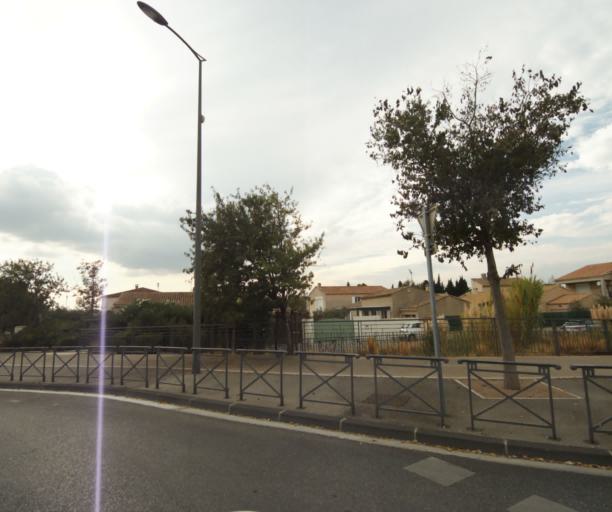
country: FR
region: Provence-Alpes-Cote d'Azur
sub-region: Departement des Bouches-du-Rhone
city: Marignane
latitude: 43.4188
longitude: 5.2026
